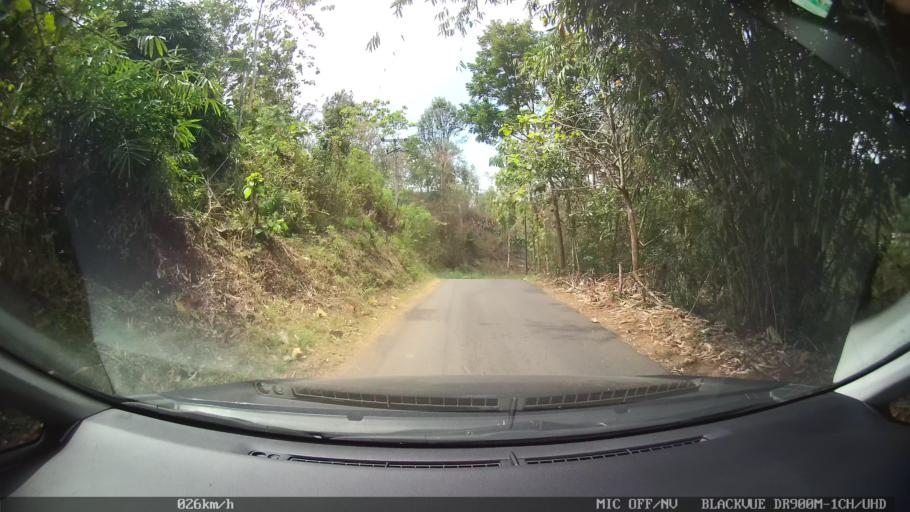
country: ID
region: Central Java
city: Candi Prambanan
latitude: -7.8180
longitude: 110.5198
